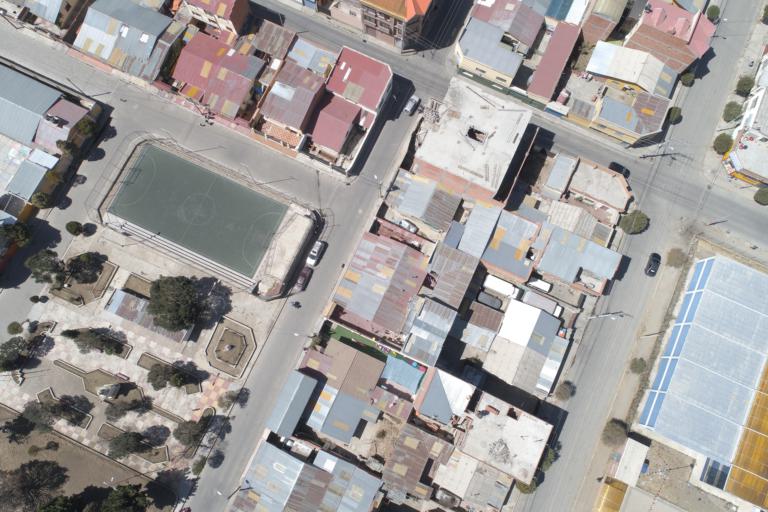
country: BO
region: La Paz
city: La Paz
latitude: -16.5318
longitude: -68.1537
